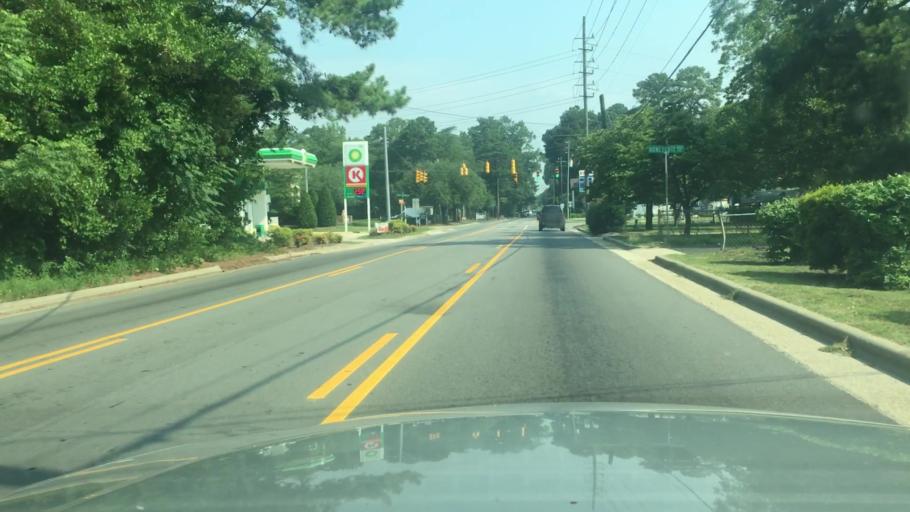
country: US
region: North Carolina
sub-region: Cumberland County
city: Hope Mills
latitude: 34.9650
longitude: -78.9437
